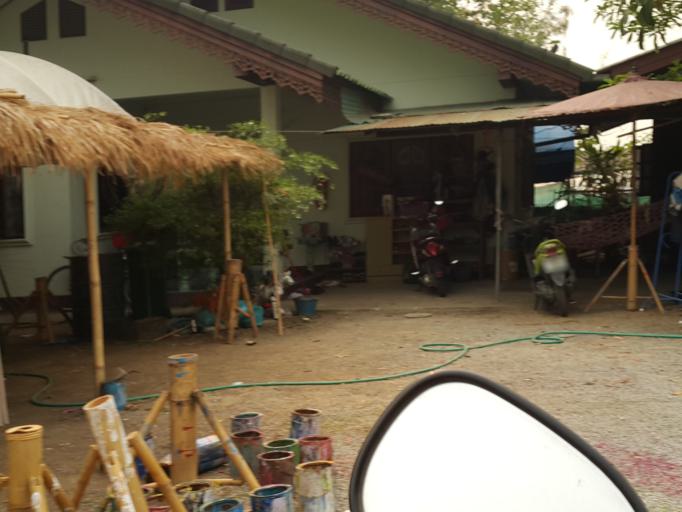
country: TH
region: Chiang Mai
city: San Kamphaeng
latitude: 18.7697
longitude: 99.0971
